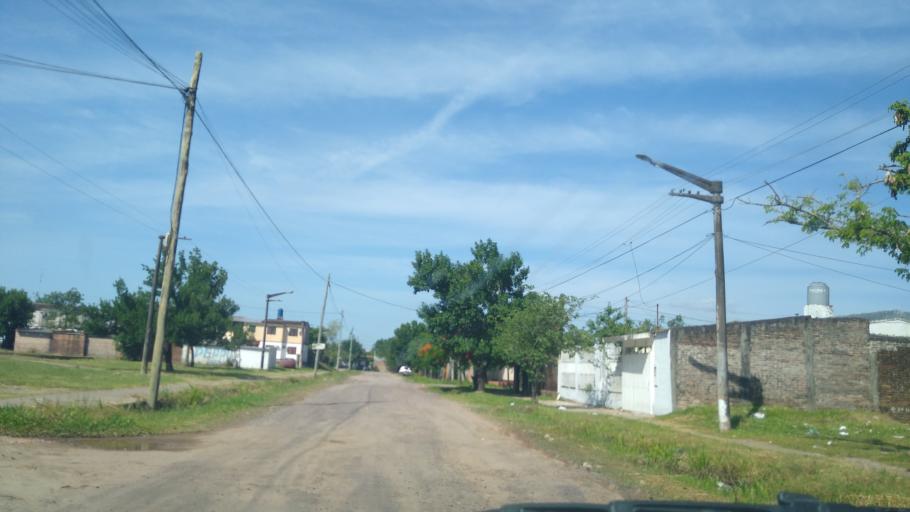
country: AR
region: Chaco
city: Puerto Vilelas
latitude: -27.4992
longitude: -58.9578
